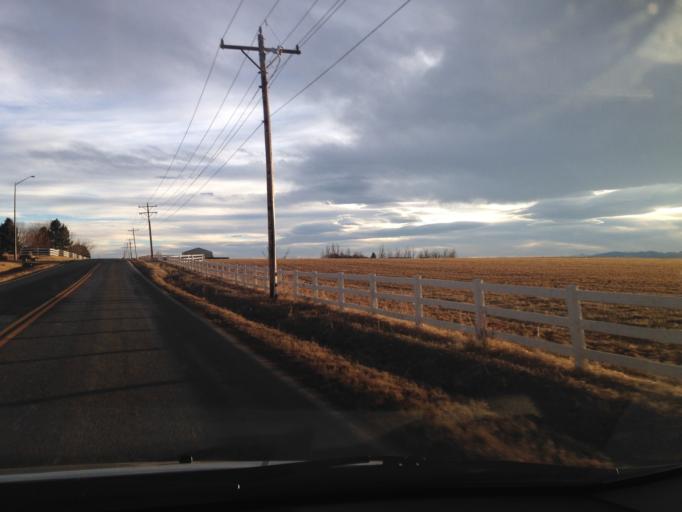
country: US
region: Colorado
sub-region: Weld County
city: Firestone
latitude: 40.1090
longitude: -104.9989
